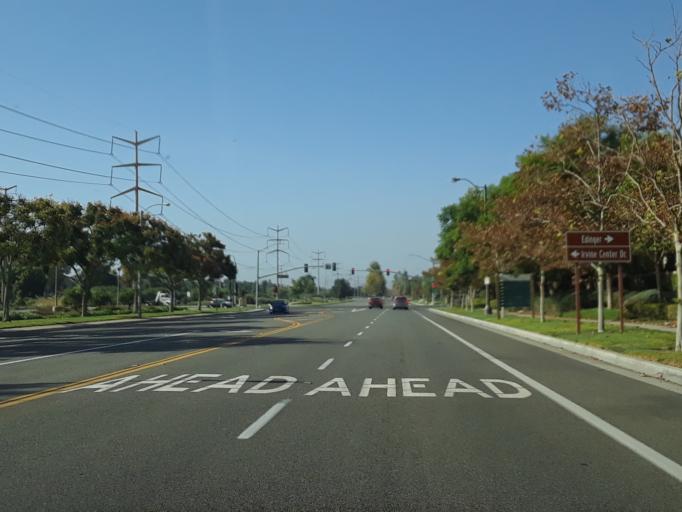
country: US
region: California
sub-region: Orange County
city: Irvine
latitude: 33.7020
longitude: -117.8017
